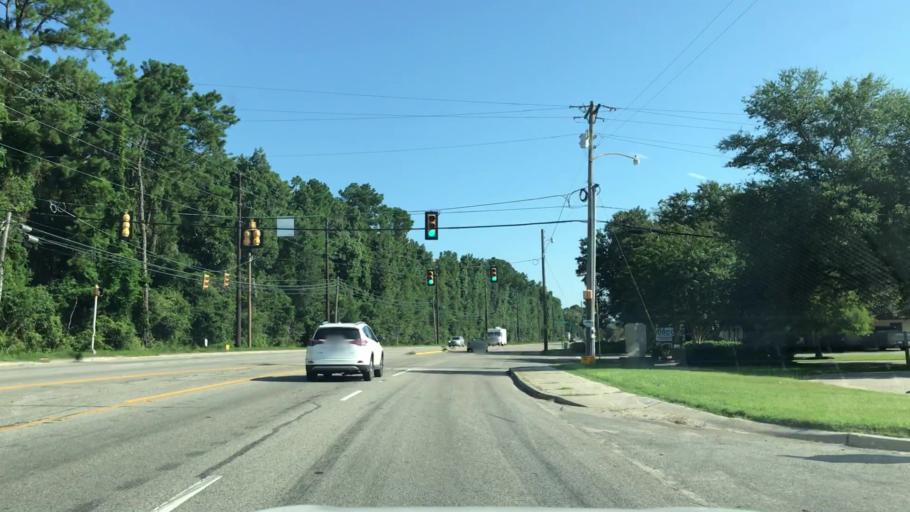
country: US
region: South Carolina
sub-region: Georgetown County
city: Georgetown
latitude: 33.4001
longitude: -79.2892
